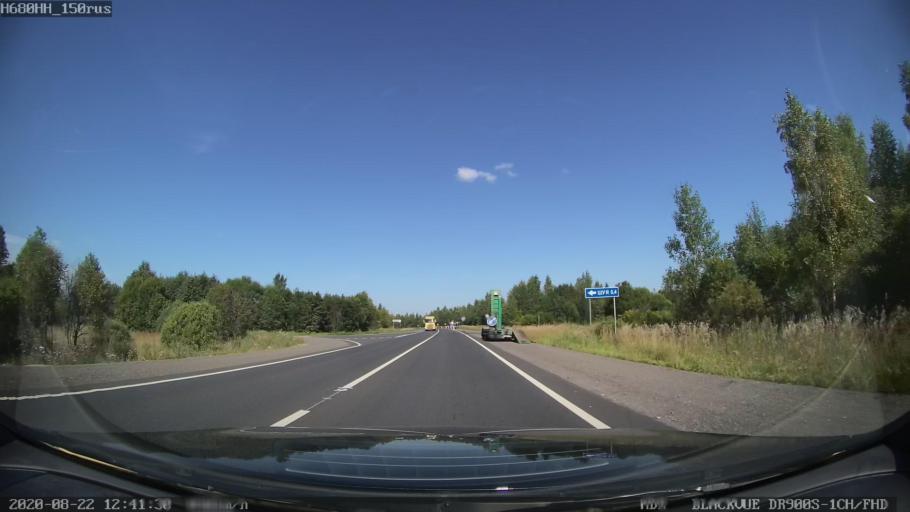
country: RU
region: Tverskaya
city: Rameshki
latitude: 57.3498
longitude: 36.0992
